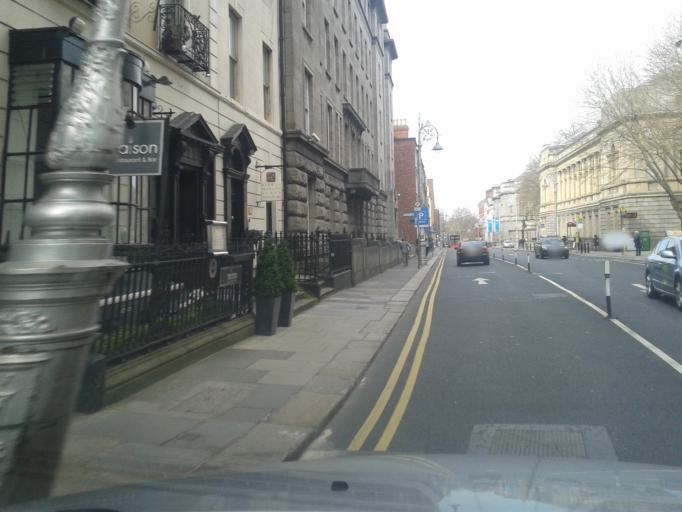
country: IE
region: Leinster
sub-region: Dublin City
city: Dublin
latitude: 53.3395
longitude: -6.2561
